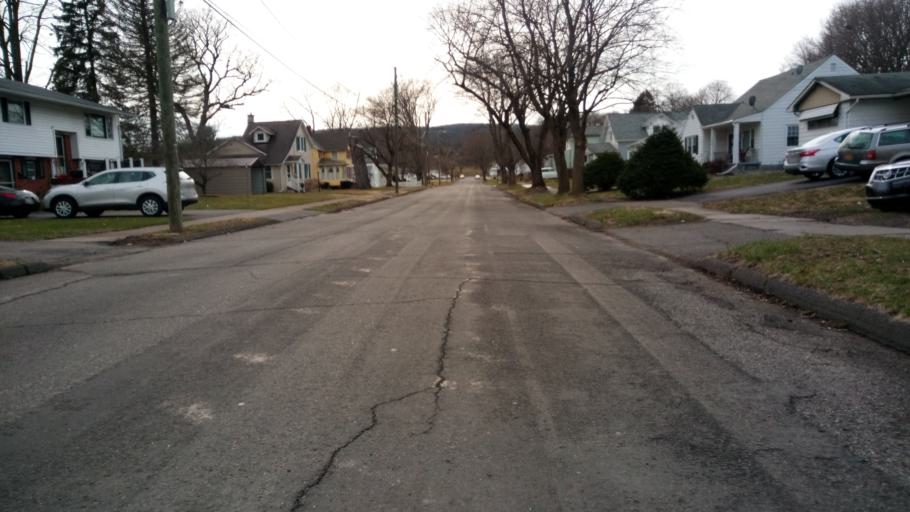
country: US
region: New York
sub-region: Chemung County
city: Elmira
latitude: 42.1072
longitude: -76.8201
